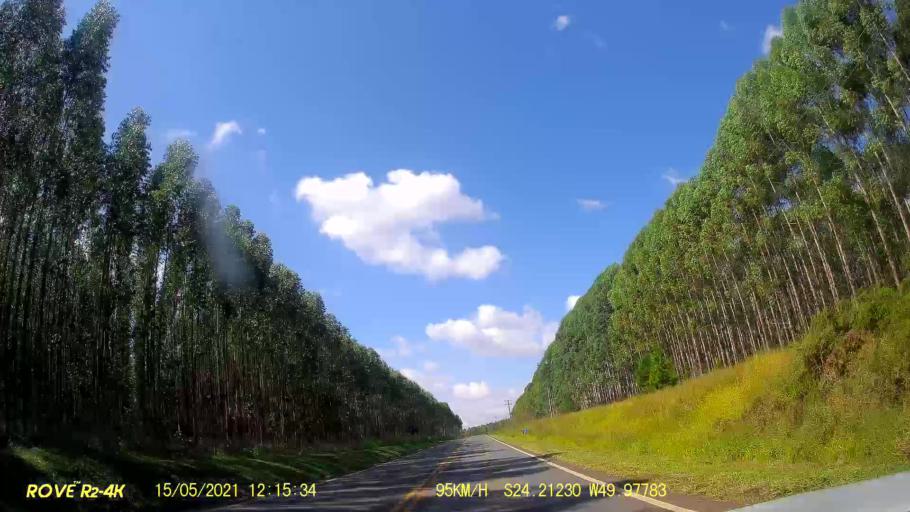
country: BR
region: Parana
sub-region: Jaguariaiva
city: Jaguariaiva
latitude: -24.2123
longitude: -49.9780
